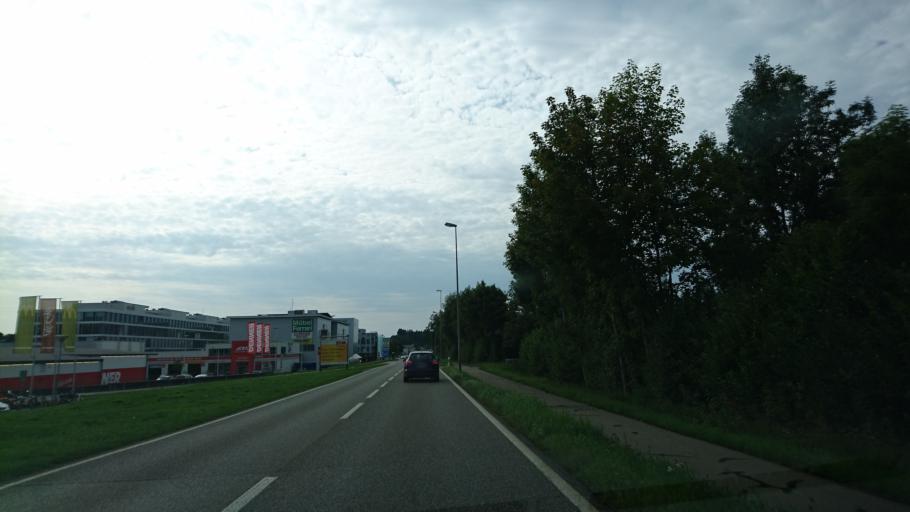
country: CH
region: Zurich
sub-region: Bezirk Hinwil
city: Hinwil
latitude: 47.3058
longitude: 8.8248
